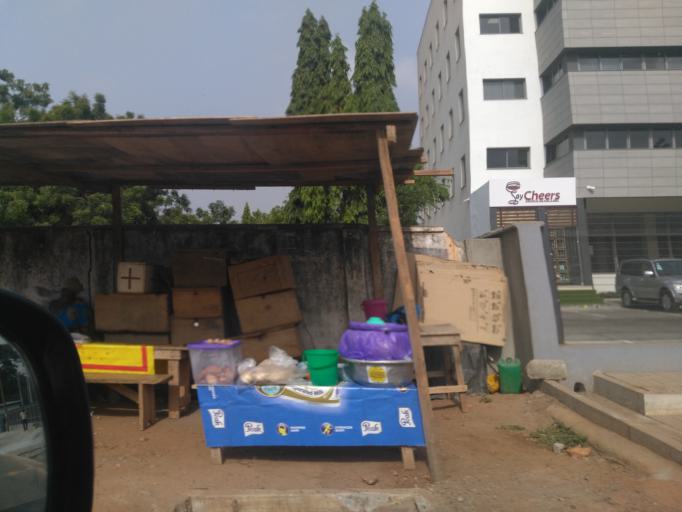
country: GH
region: Greater Accra
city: Accra
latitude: 5.6071
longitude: -0.1854
